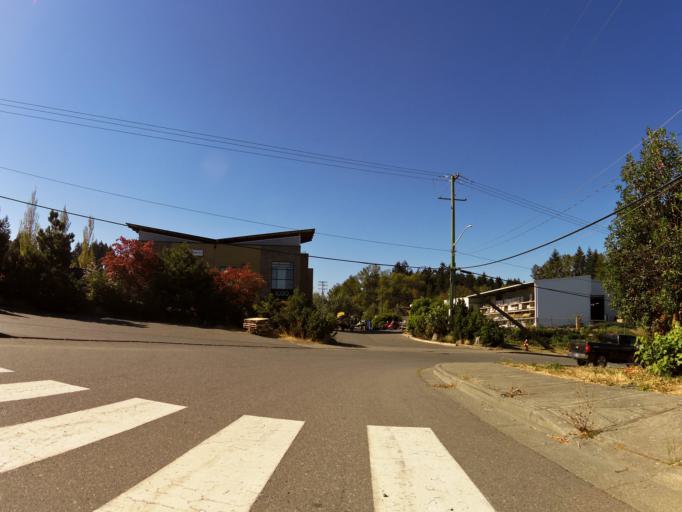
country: CA
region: British Columbia
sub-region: Cowichan Valley Regional District
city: Ladysmith
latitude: 48.9988
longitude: -123.8223
